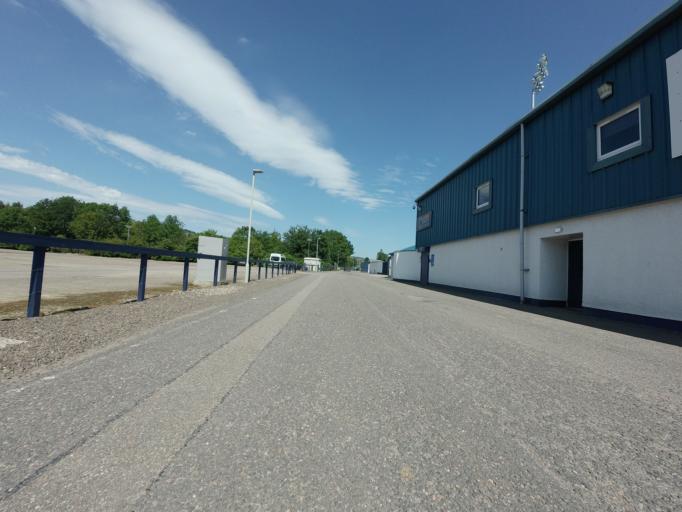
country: GB
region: Scotland
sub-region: Highland
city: Dingwall
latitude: 57.5962
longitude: -4.4199
